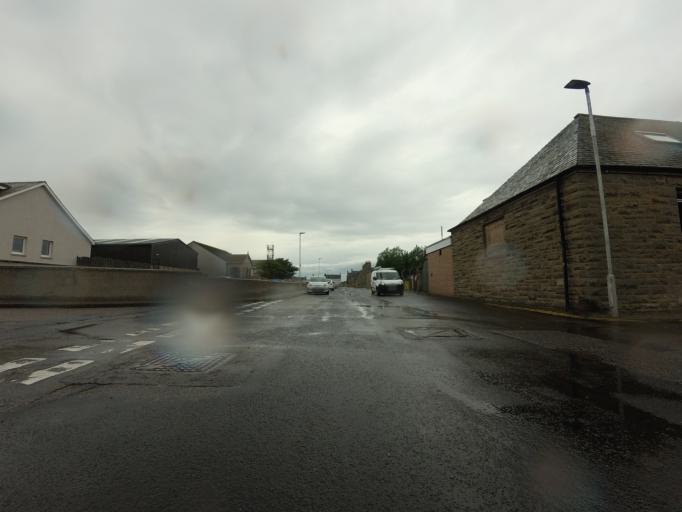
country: GB
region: Scotland
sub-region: Moray
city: Buckie
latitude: 57.6768
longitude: -2.9604
